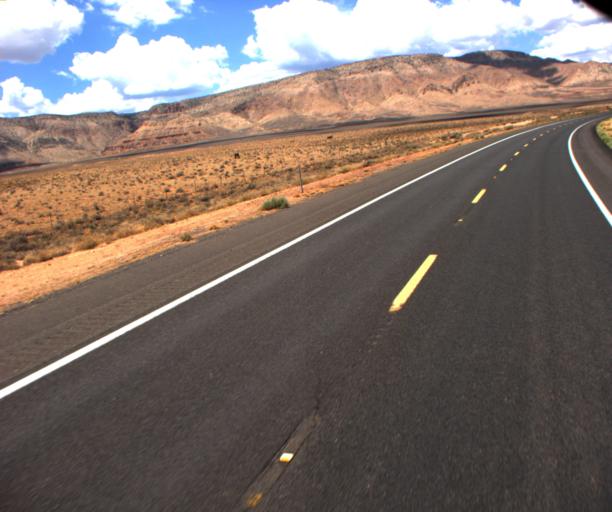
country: US
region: Arizona
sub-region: Coconino County
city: Tuba City
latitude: 35.8758
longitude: -111.5163
